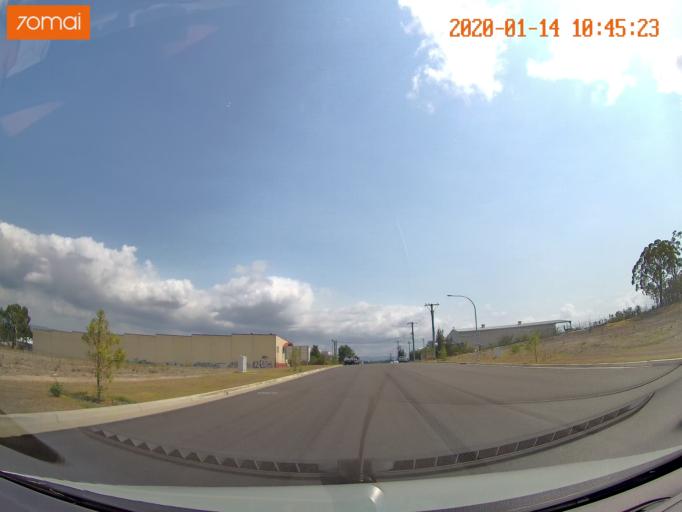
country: AU
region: New South Wales
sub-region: Lake Macquarie Shire
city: Dora Creek
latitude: -33.1215
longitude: 151.4727
